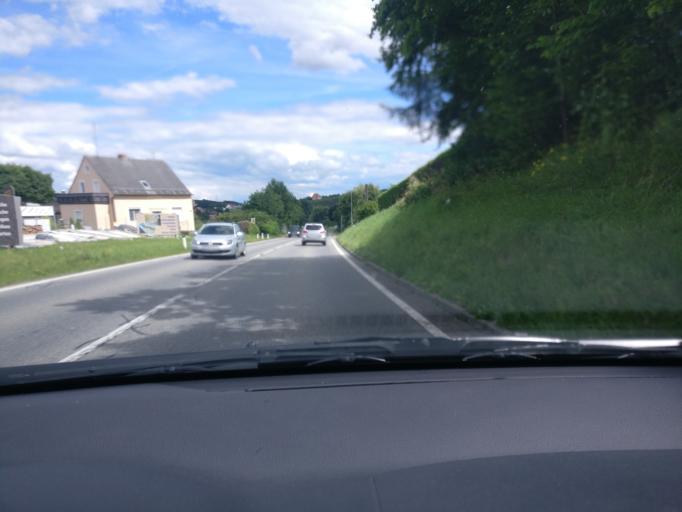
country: AT
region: Styria
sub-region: Politischer Bezirk Weiz
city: Hirnsdorf
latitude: 47.1727
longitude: 15.7969
